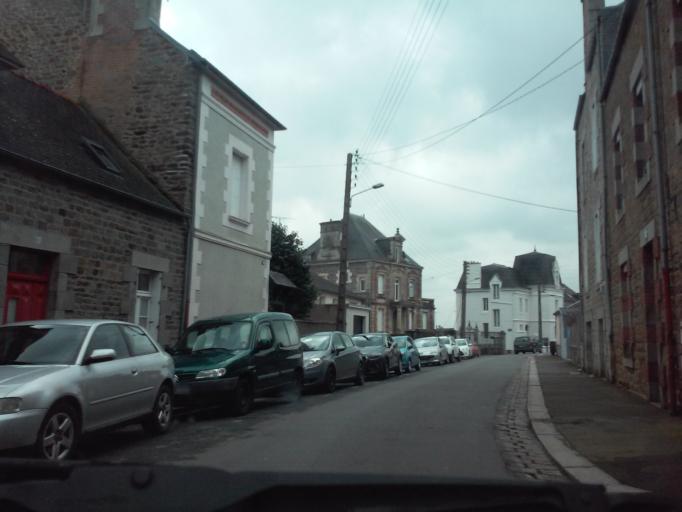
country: FR
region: Brittany
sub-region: Departement d'Ille-et-Vilaine
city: Fougeres
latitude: 48.3575
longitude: -1.1926
